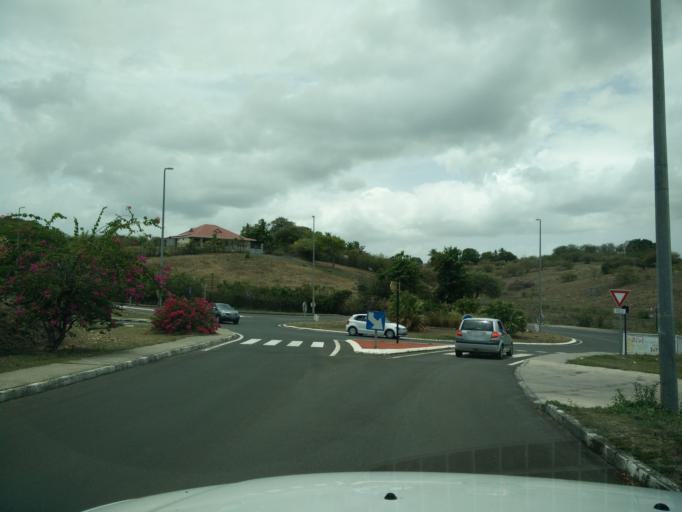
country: GP
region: Guadeloupe
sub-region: Guadeloupe
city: Sainte-Anne
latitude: 16.2483
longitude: -61.3586
